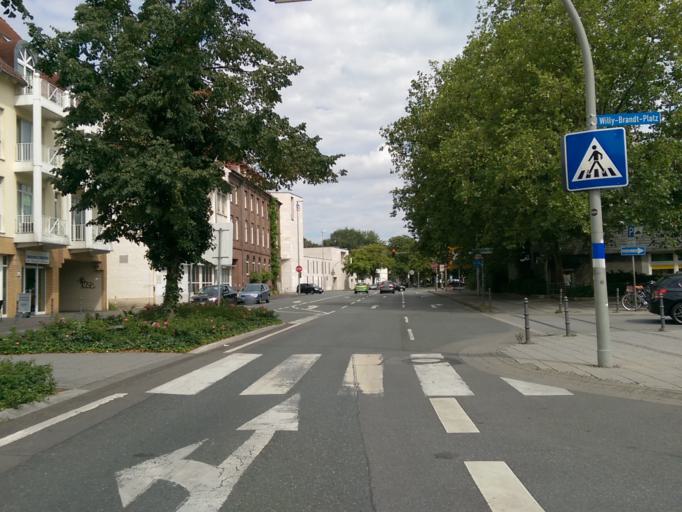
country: DE
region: North Rhine-Westphalia
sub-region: Regierungsbezirk Detmold
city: Guetersloh
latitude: 51.9079
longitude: 8.3843
